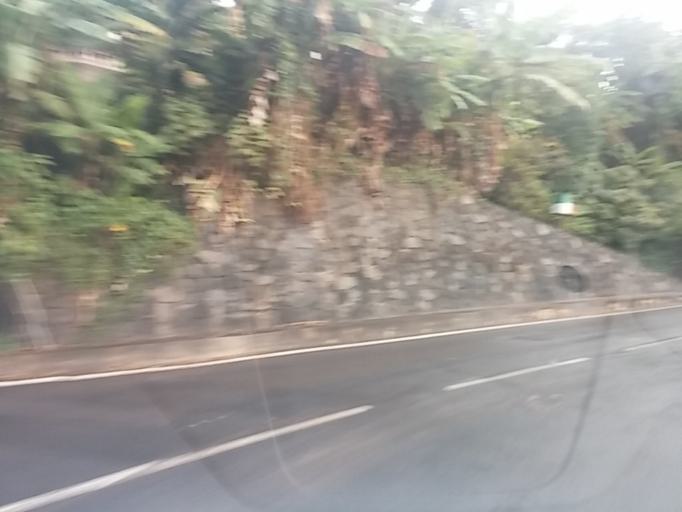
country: RE
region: Reunion
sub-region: Reunion
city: Saint-Denis
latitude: -20.8990
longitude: 55.4184
